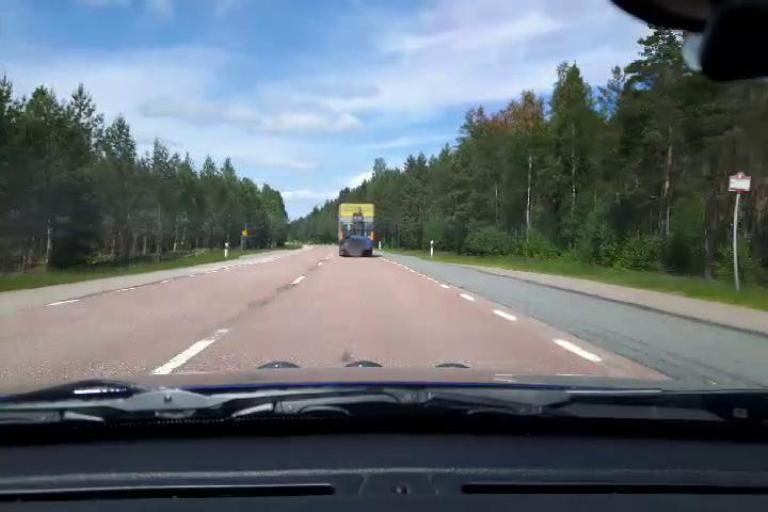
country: SE
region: Uppsala
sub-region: Osthammars Kommun
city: Bjorklinge
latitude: 60.1310
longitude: 17.5093
